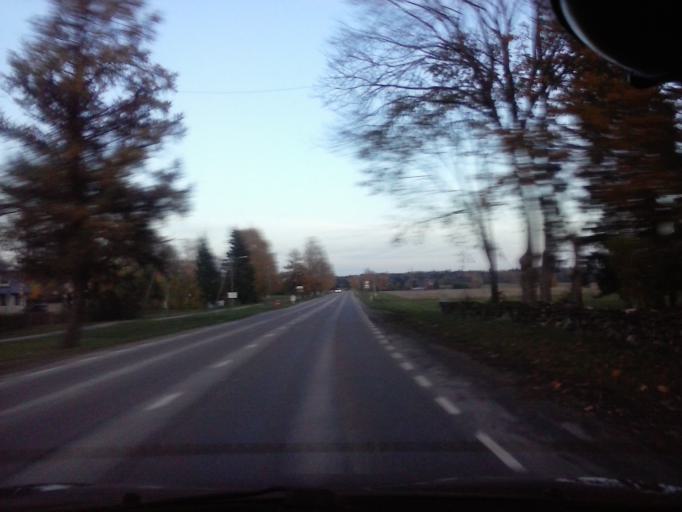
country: EE
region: Raplamaa
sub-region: Maerjamaa vald
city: Marjamaa
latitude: 58.9167
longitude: 24.4386
